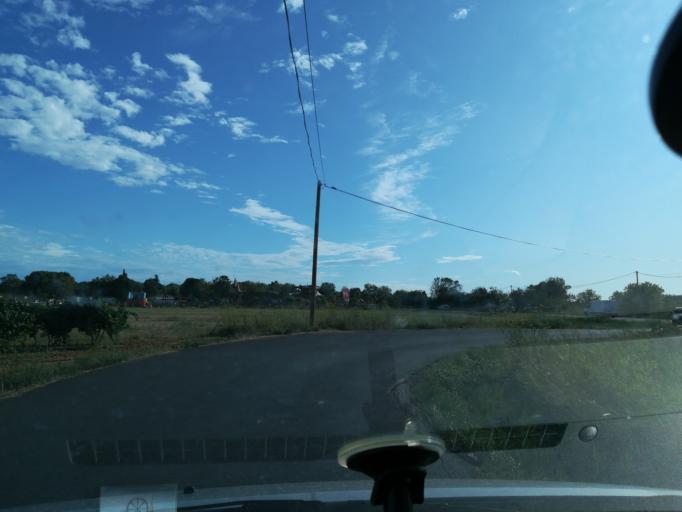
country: FR
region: Languedoc-Roussillon
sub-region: Departement de l'Herault
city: Vias
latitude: 43.2989
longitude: 3.4020
